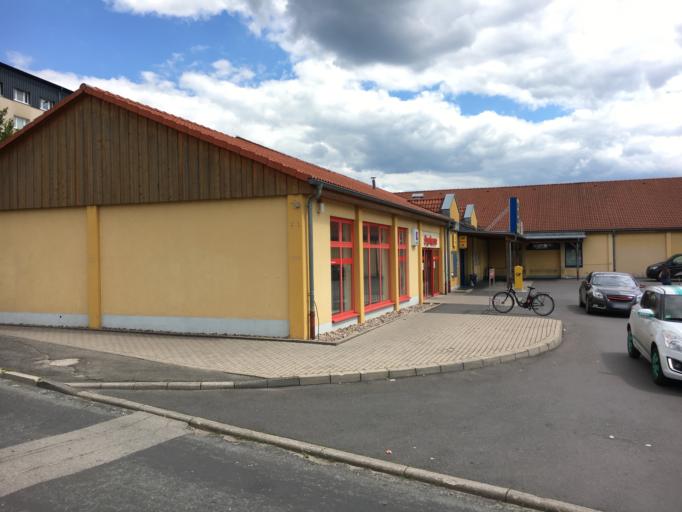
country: DE
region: Thuringia
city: Schmalkalden
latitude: 50.7187
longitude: 10.4661
